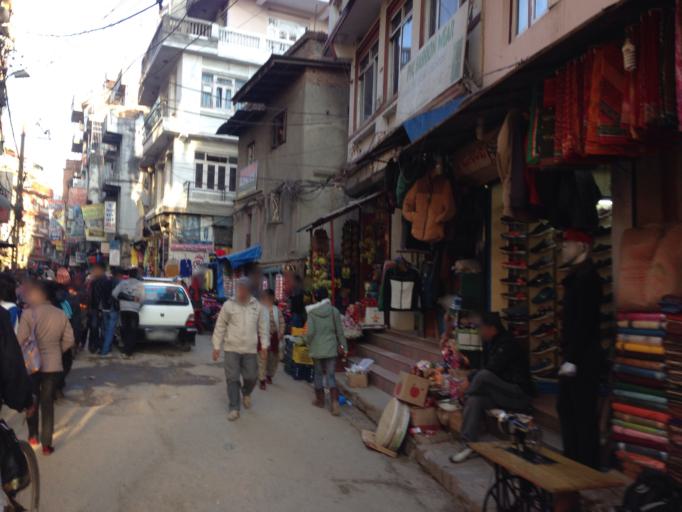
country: NP
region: Central Region
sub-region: Bagmati Zone
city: Kathmandu
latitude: 27.7168
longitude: 85.3451
